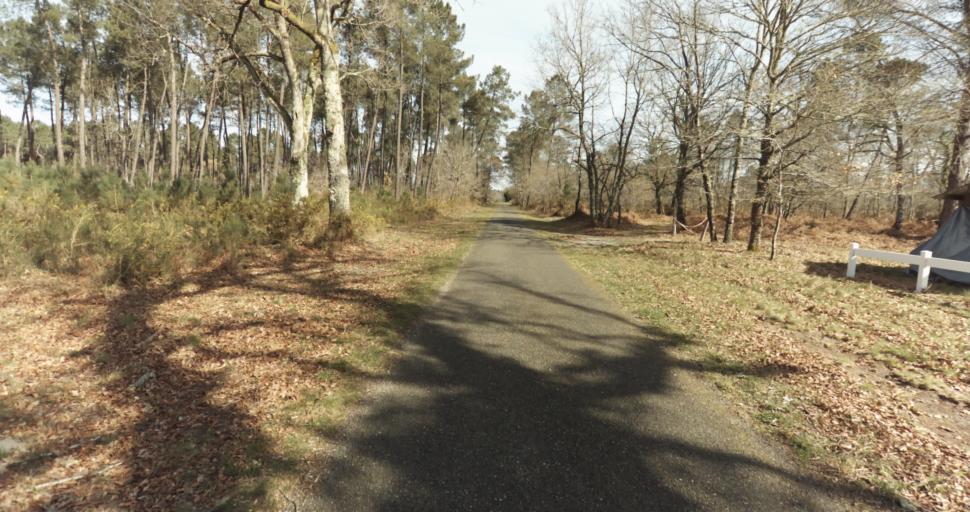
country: FR
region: Aquitaine
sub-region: Departement des Landes
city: Roquefort
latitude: 44.0730
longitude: -0.3568
